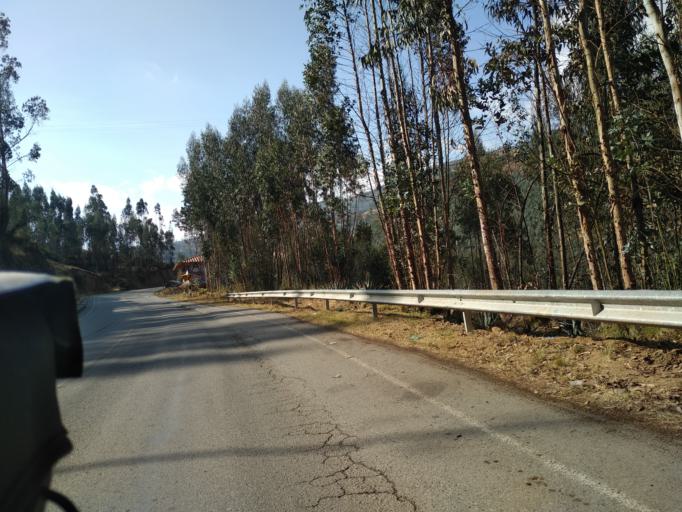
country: PE
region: La Libertad
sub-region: Provincia de Otuzco
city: Mache
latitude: -7.9982
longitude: -78.5081
